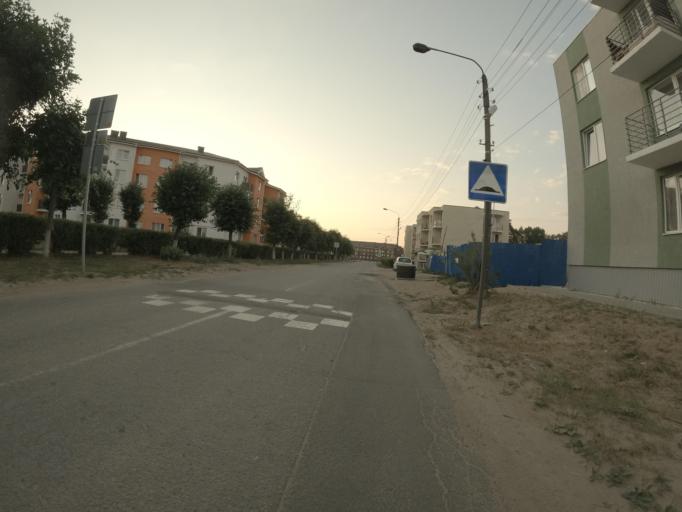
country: RU
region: Leningrad
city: Pavlovo
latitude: 59.8465
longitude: 30.9363
